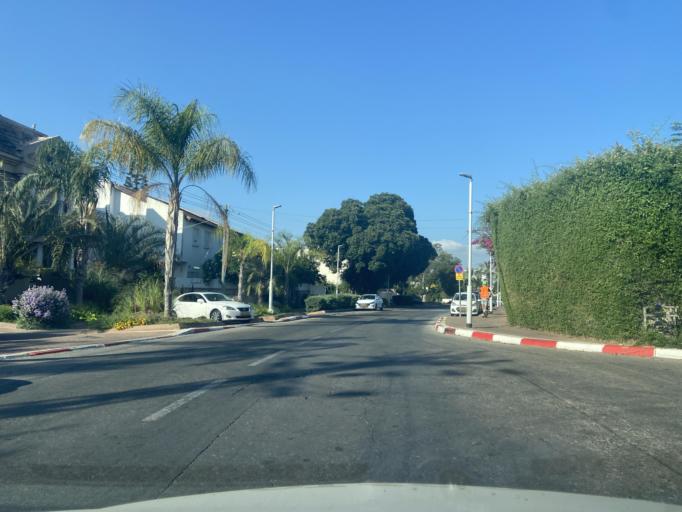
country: IL
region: Central District
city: Yehud
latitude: 32.0390
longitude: 34.8937
